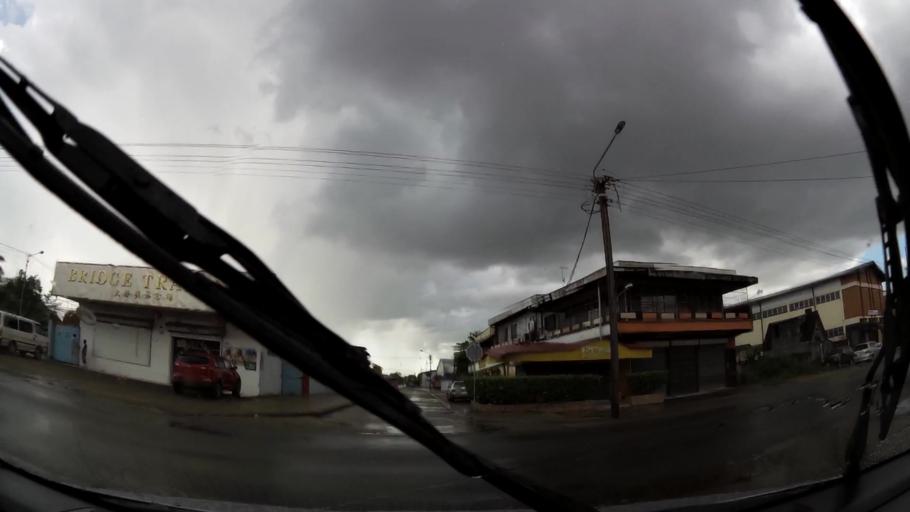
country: SR
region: Paramaribo
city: Paramaribo
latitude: 5.8231
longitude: -55.1670
